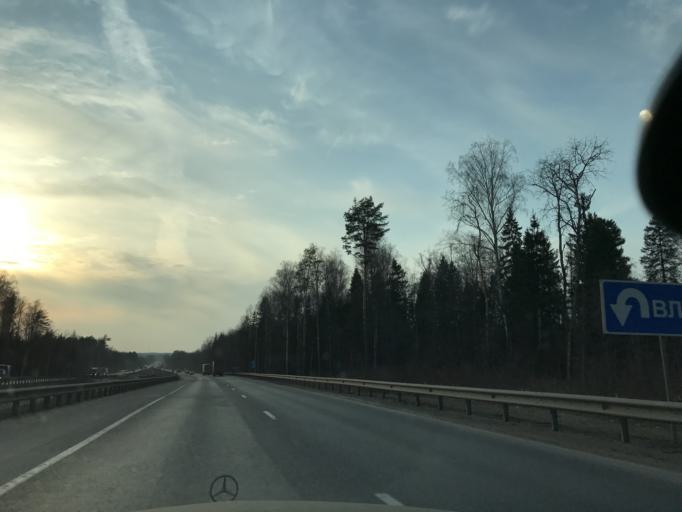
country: RU
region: Vladimir
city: Kosterevo
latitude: 55.9588
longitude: 39.6653
